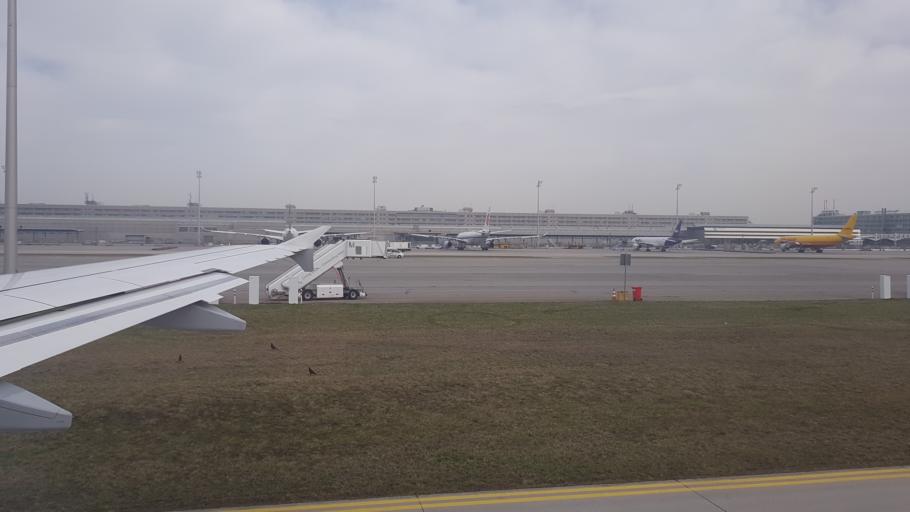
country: DE
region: Bavaria
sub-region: Upper Bavaria
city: Hallbergmoos
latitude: 48.3457
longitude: 11.7691
